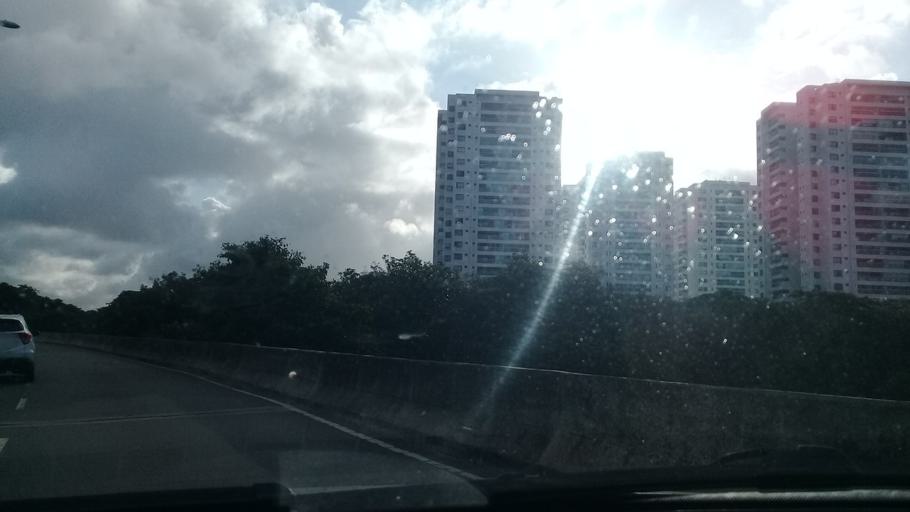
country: BR
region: Pernambuco
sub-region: Recife
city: Recife
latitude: -8.1107
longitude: -34.9008
